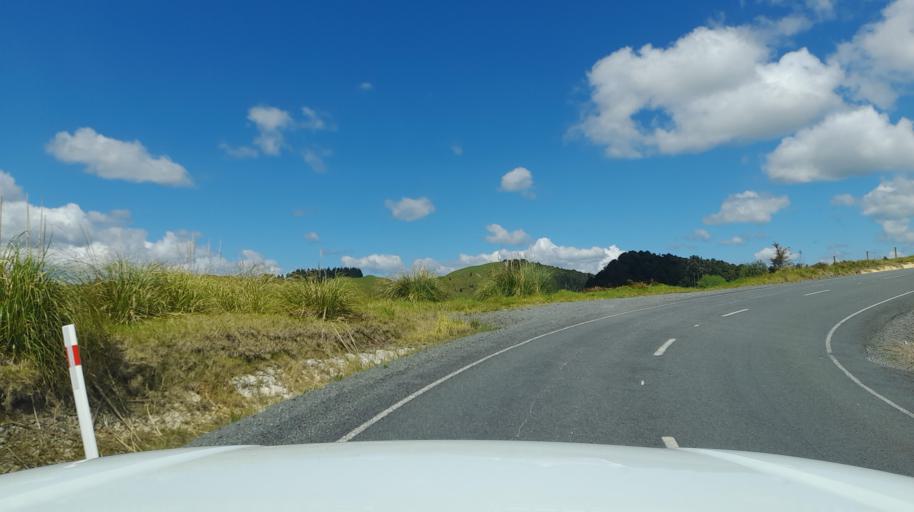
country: NZ
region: Northland
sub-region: Far North District
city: Taipa
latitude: -35.1064
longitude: 173.4610
